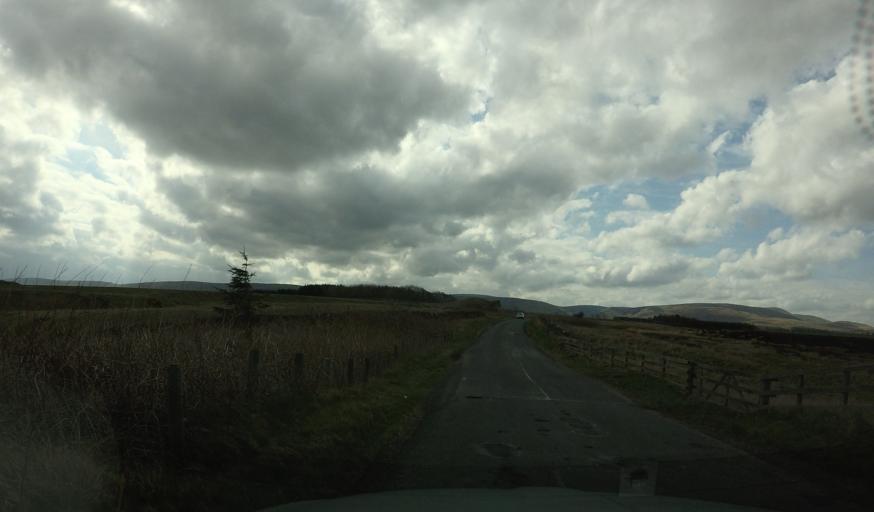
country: GB
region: Scotland
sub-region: Midlothian
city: Bonnyrigg
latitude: 55.7850
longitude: -3.1308
